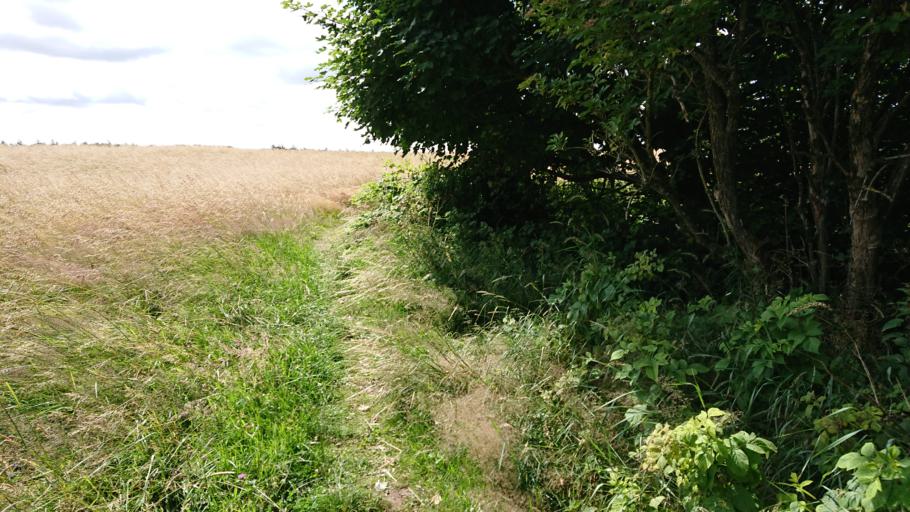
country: DK
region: North Denmark
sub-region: Jammerbugt Kommune
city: Brovst
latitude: 57.1316
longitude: 9.4057
